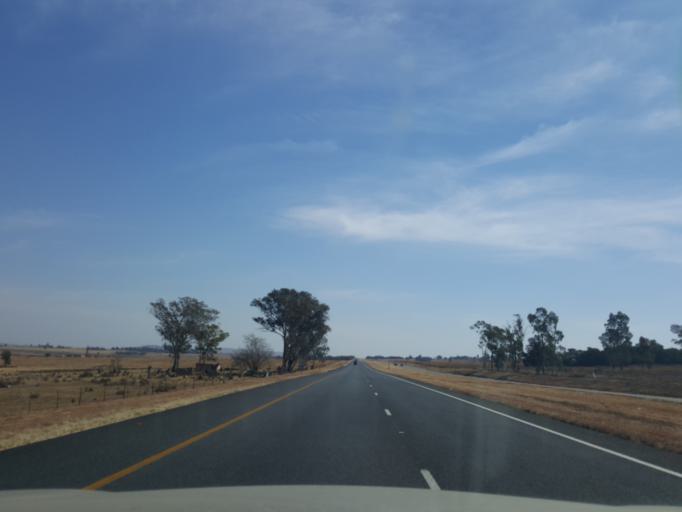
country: ZA
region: Gauteng
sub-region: City of Tshwane Metropolitan Municipality
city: Bronkhorstspruit
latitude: -25.8000
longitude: 28.6604
